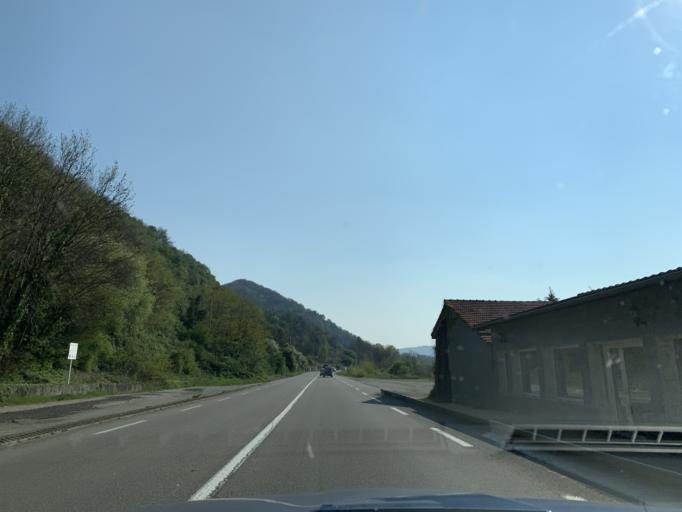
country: FR
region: Rhone-Alpes
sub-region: Departement de la Drome
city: Saint-Vallier
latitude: 45.1528
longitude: 4.8314
